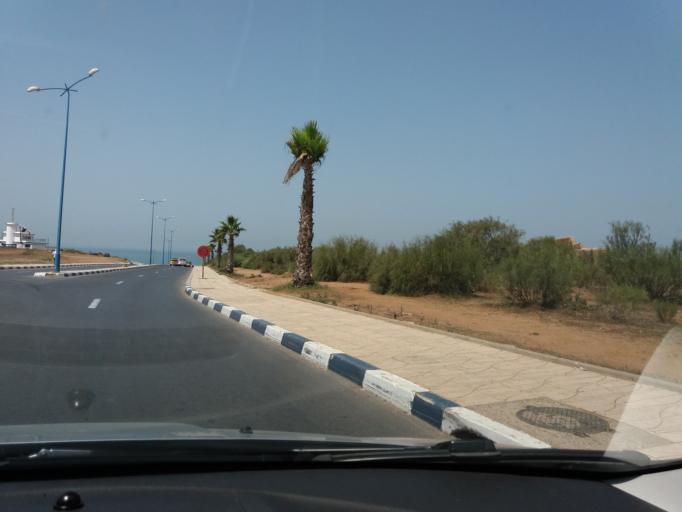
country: MA
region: Gharb-Chrarda-Beni Hssen
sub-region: Kenitra Province
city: Kenitra
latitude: 34.2631
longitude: -6.6572
